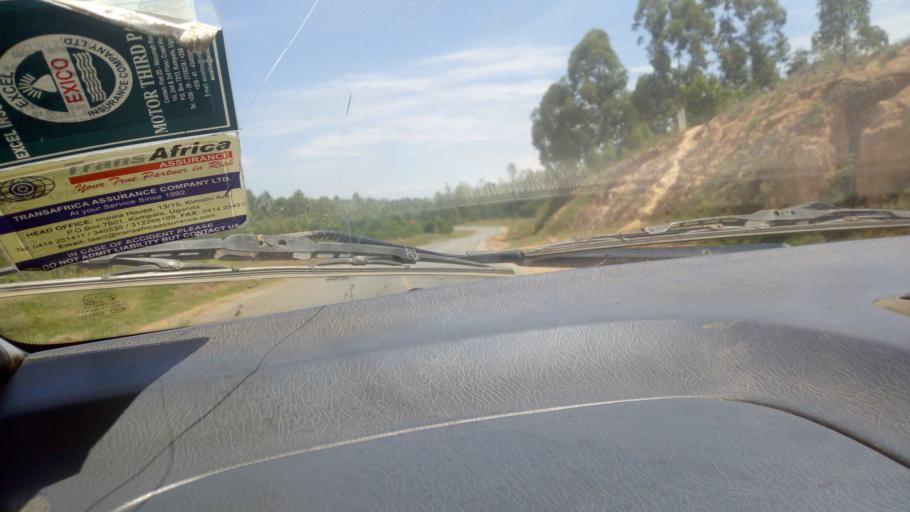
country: UG
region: Western Region
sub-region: Buhweju District
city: Buhweju
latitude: -0.2792
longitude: 30.5614
